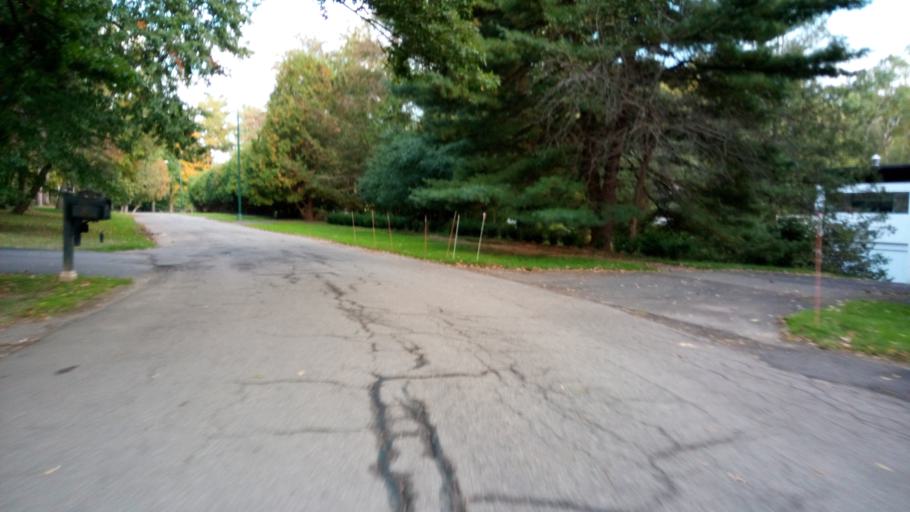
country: US
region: New York
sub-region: Chemung County
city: West Elmira
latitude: 42.0911
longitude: -76.8332
